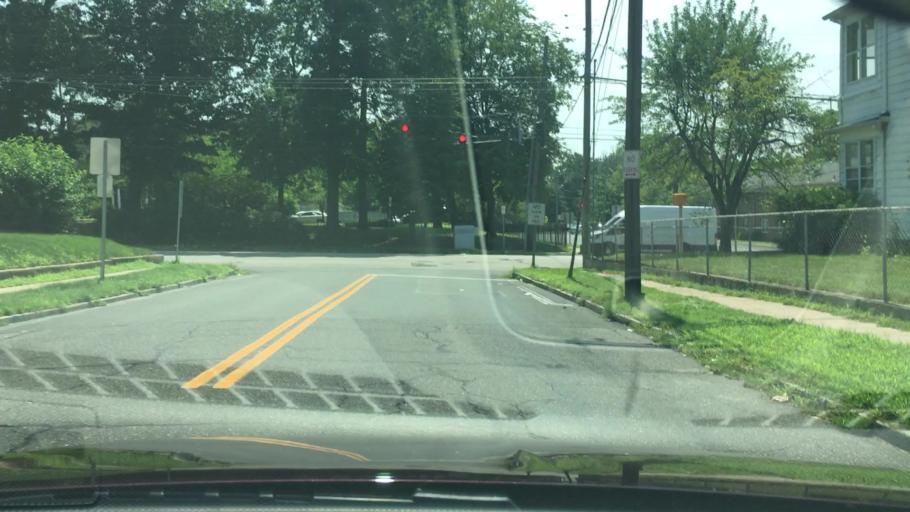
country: US
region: Connecticut
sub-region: Hartford County
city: East Hartford
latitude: 41.7801
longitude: -72.6073
